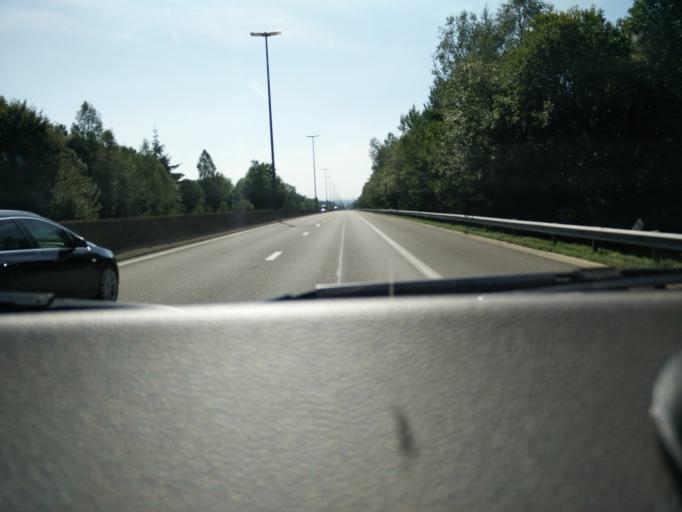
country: BE
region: Wallonia
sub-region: Province du Luxembourg
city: Leglise
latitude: 49.7558
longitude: 5.5645
